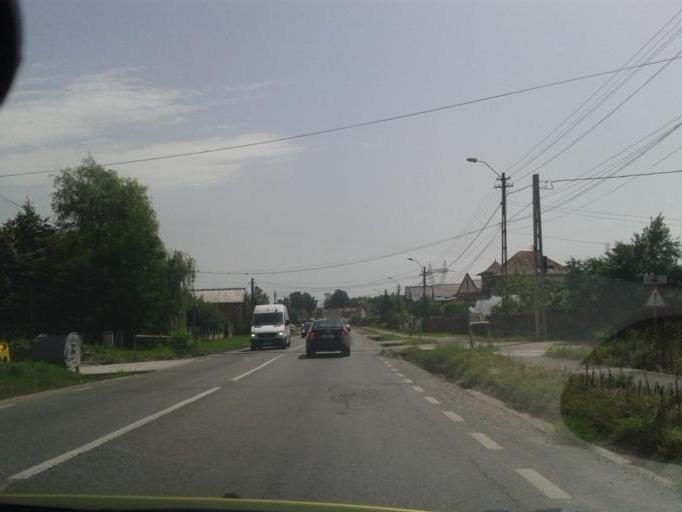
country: RO
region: Arges
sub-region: Comuna Bascov
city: Bascov
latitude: 44.8856
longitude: 24.8044
